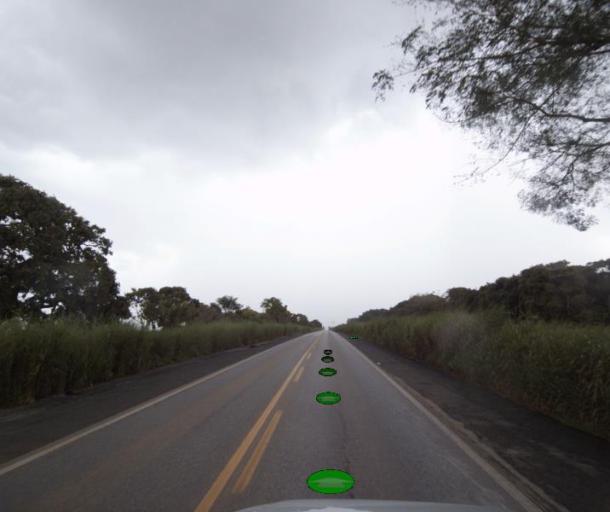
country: BR
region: Goias
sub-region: Uruacu
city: Uruacu
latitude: -14.2104
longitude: -49.1306
